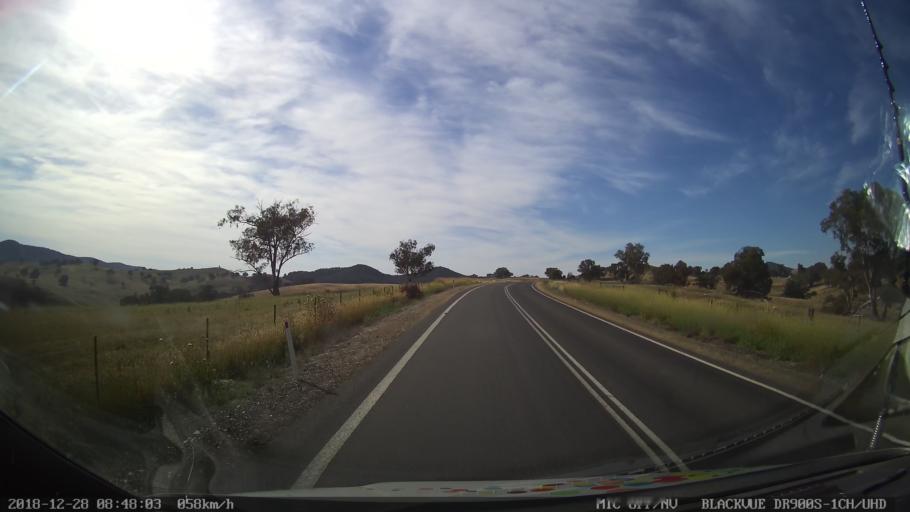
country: AU
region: New South Wales
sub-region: Upper Lachlan Shire
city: Crookwell
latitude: -34.0322
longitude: 149.3362
